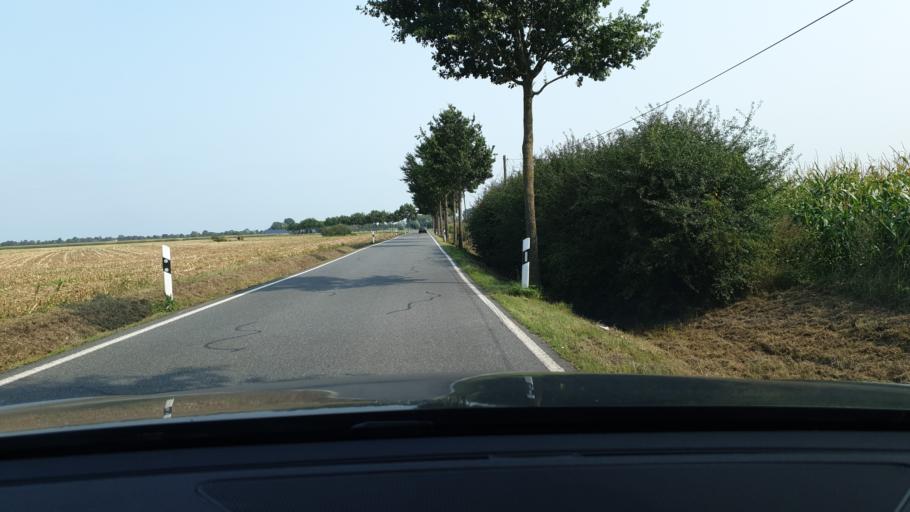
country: DE
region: North Rhine-Westphalia
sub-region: Regierungsbezirk Dusseldorf
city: Kranenburg
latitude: 51.8466
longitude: 6.0439
